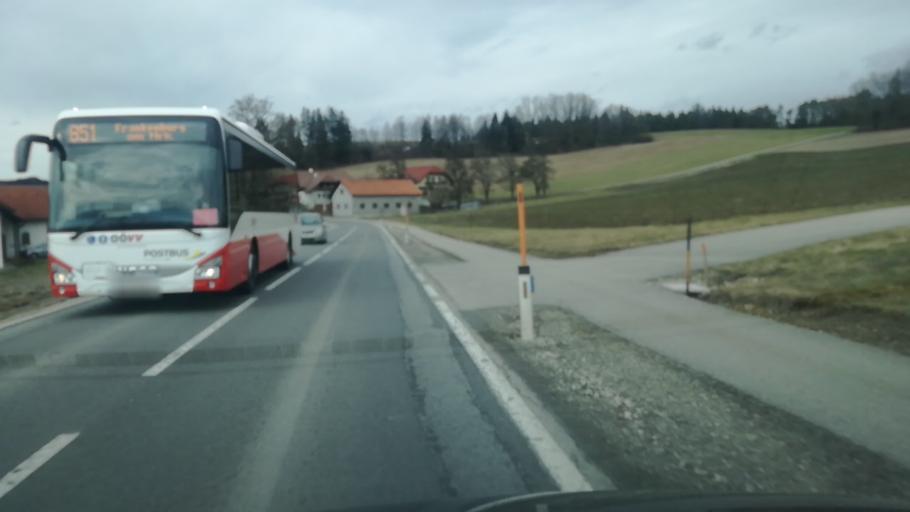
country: AT
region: Upper Austria
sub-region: Politischer Bezirk Vocklabruck
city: Frankenburg
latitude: 48.0786
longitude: 13.4888
